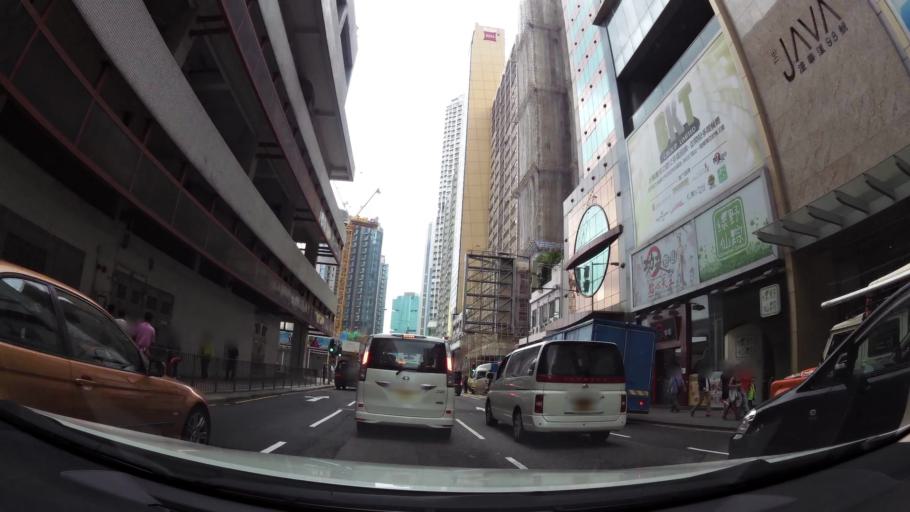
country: HK
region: Wanchai
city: Wan Chai
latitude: 22.2922
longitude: 114.1996
